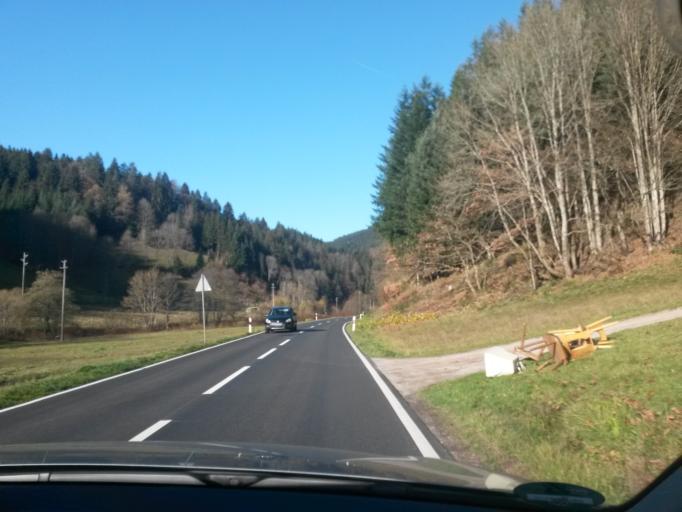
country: DE
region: Baden-Wuerttemberg
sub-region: Karlsruhe Region
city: Bad Rippoldsau-Schapbach
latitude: 48.3981
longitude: 8.3134
